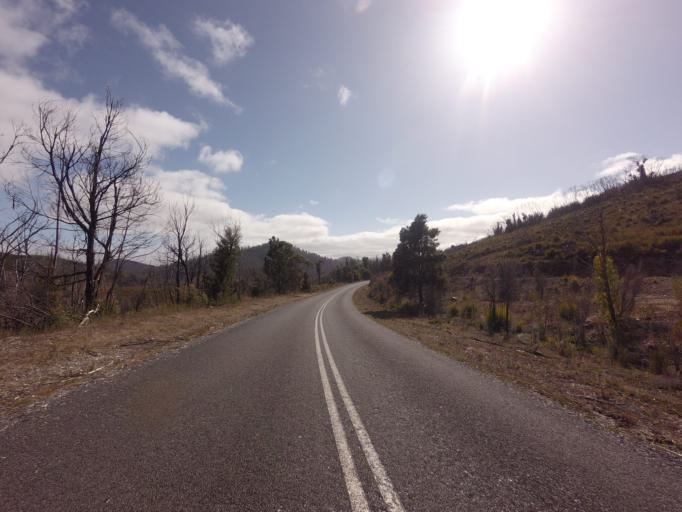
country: AU
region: Tasmania
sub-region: Huon Valley
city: Geeveston
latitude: -42.8506
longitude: 146.2353
